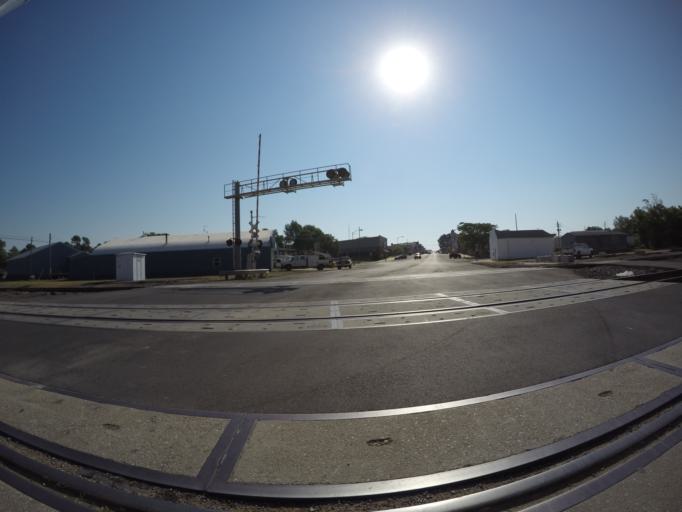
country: US
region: Kansas
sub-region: Brown County
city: Hiawatha
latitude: 39.8529
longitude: -95.5416
